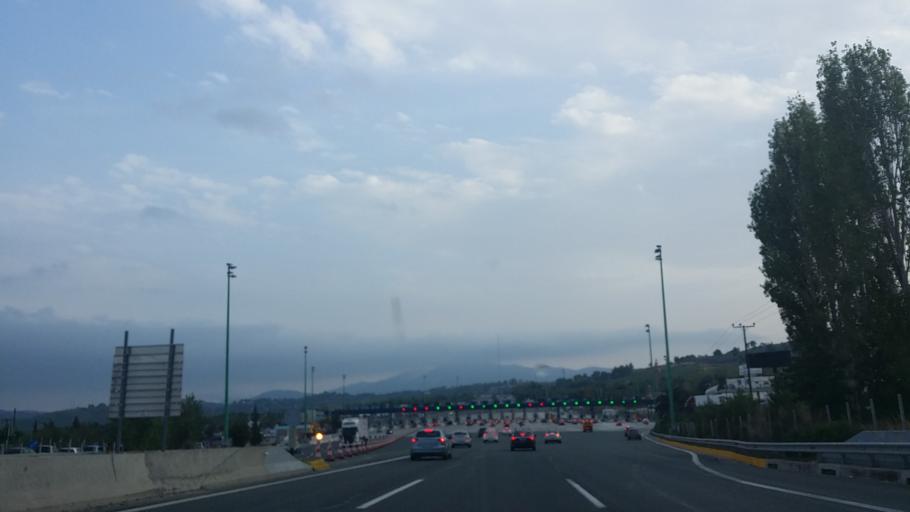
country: GR
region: Attica
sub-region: Nomarchia Anatolikis Attikis
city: Afidnes
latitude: 38.1797
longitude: 23.8533
